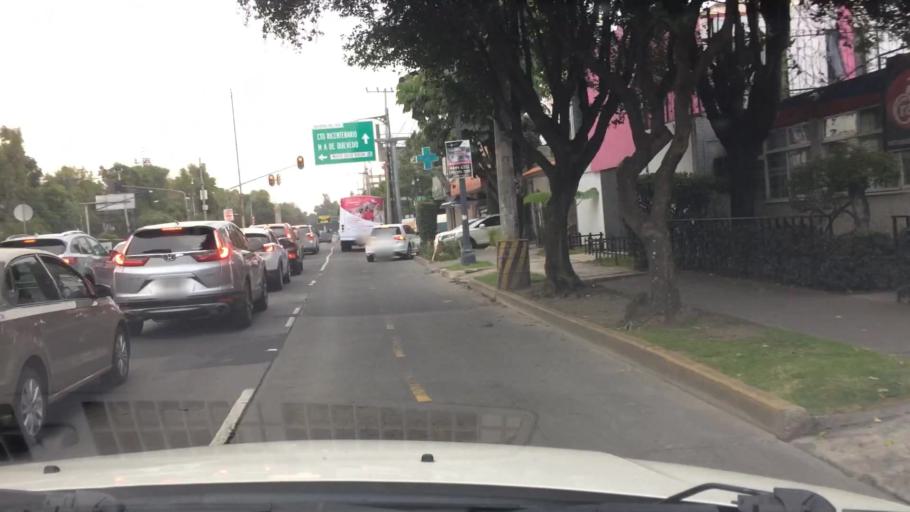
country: MX
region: Mexico City
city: Coyoacan
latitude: 19.3271
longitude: -99.1409
